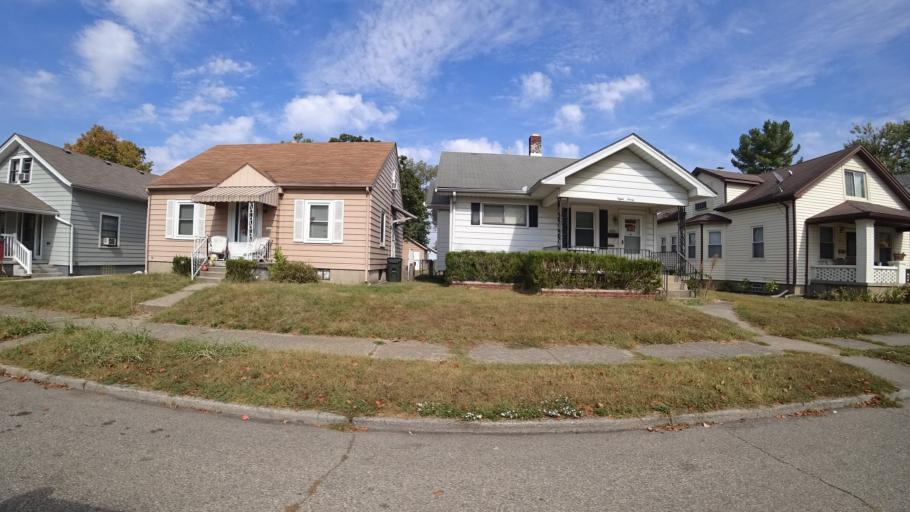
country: US
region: Ohio
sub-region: Butler County
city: Fairfield
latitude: 39.3611
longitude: -84.5536
